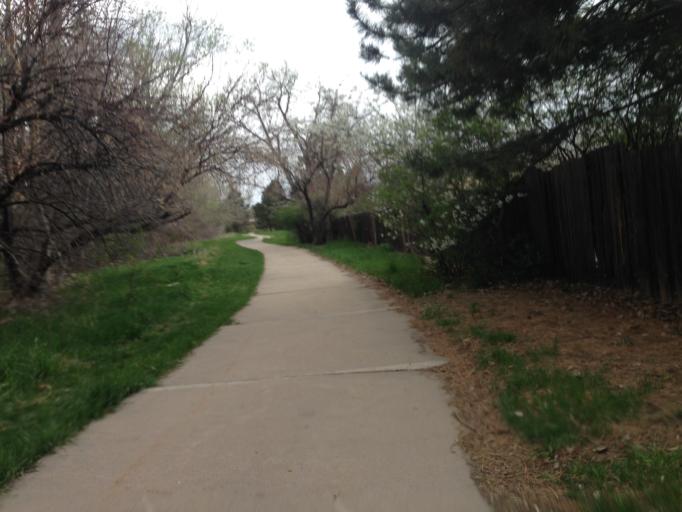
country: US
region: Colorado
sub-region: Boulder County
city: Louisville
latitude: 39.9891
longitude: -105.1358
